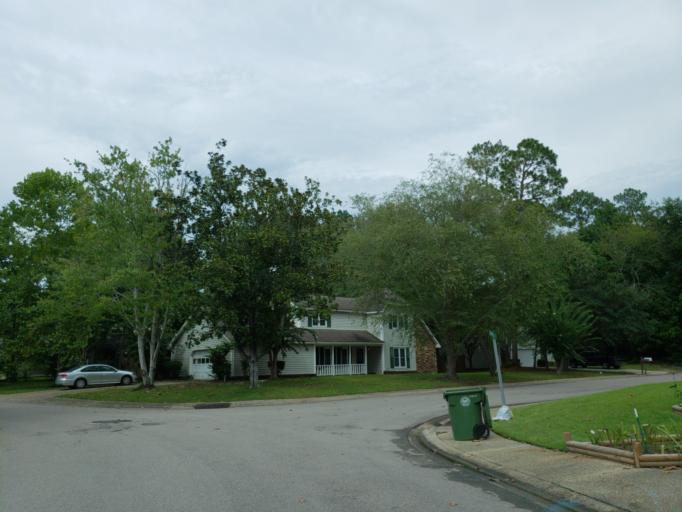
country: US
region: Mississippi
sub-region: Lamar County
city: West Hattiesburg
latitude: 31.3152
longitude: -89.3501
